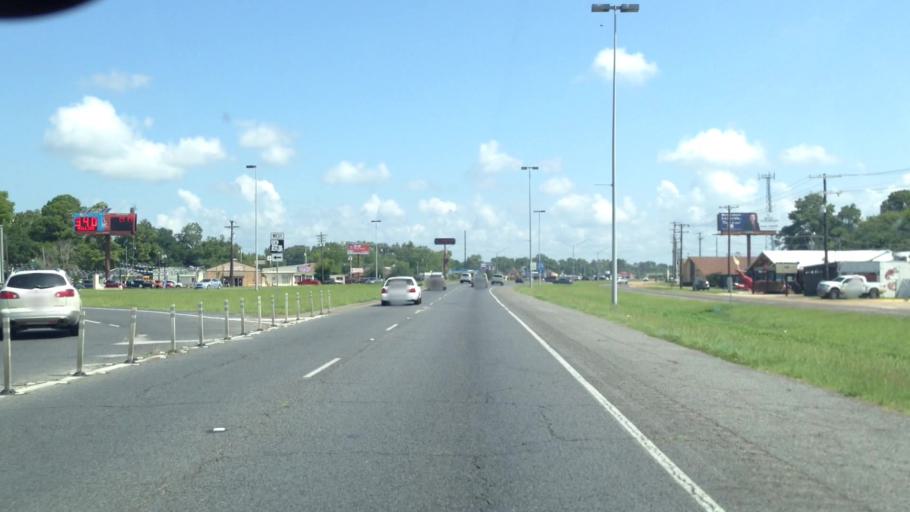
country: US
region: Louisiana
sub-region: Rapides Parish
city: Alexandria
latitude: 31.3005
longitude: -92.4798
